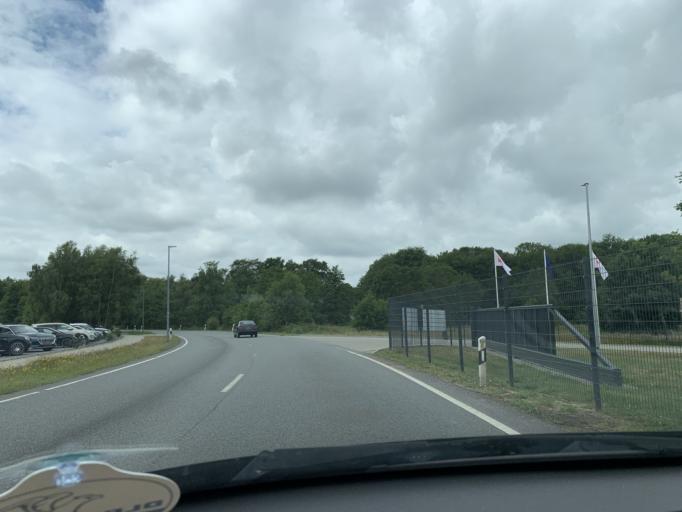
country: DE
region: Lower Saxony
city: Varel
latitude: 53.3955
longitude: 8.1135
